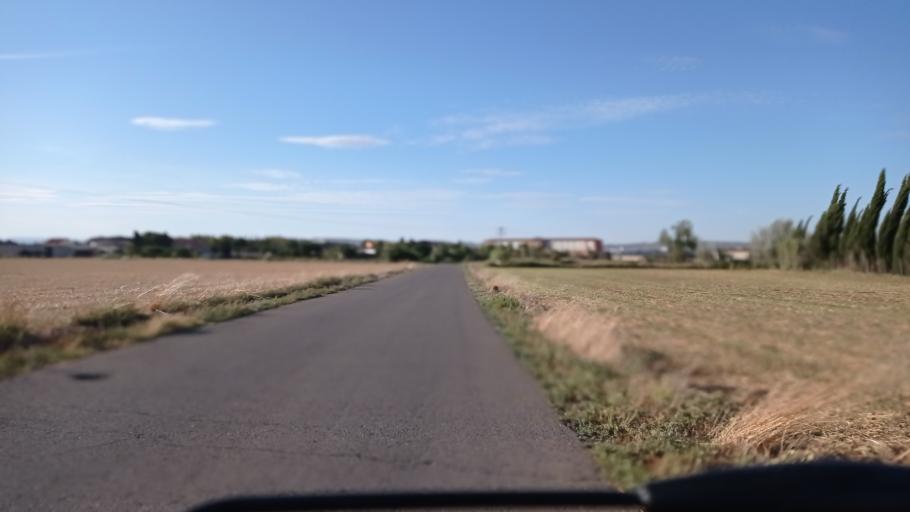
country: ES
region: Aragon
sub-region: Provincia de Zaragoza
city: Oliver-Valdefierro, Oliver, Valdefierro
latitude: 41.6736
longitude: -0.9666
